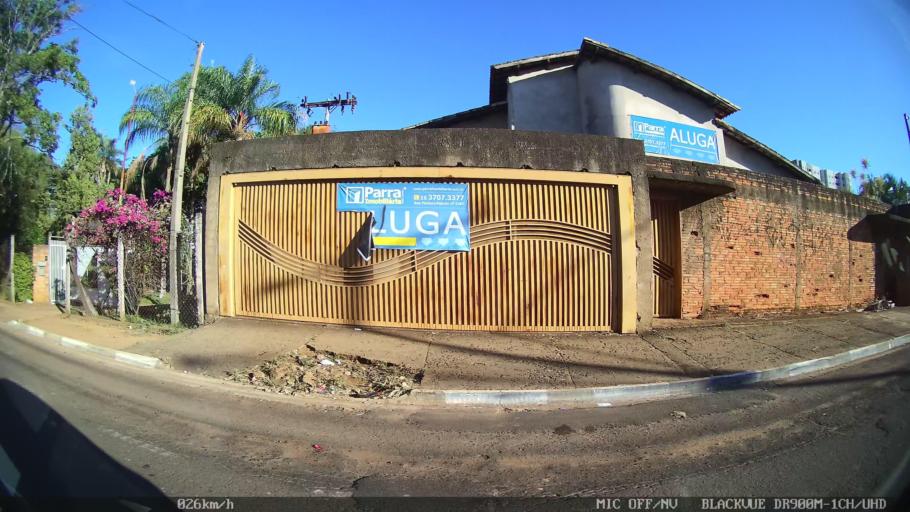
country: BR
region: Sao Paulo
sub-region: Franca
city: Franca
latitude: -20.5660
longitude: -47.4037
